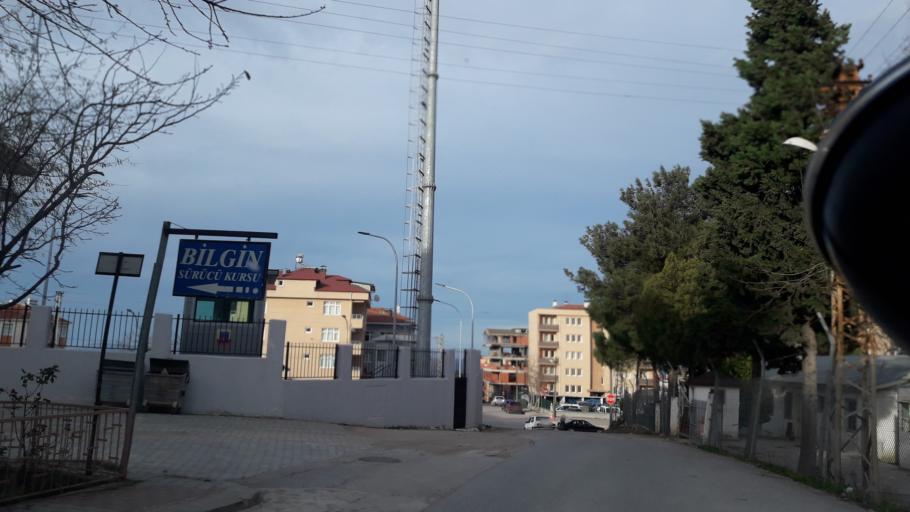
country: TR
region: Sinop
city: Gerze
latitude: 41.8067
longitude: 35.1863
